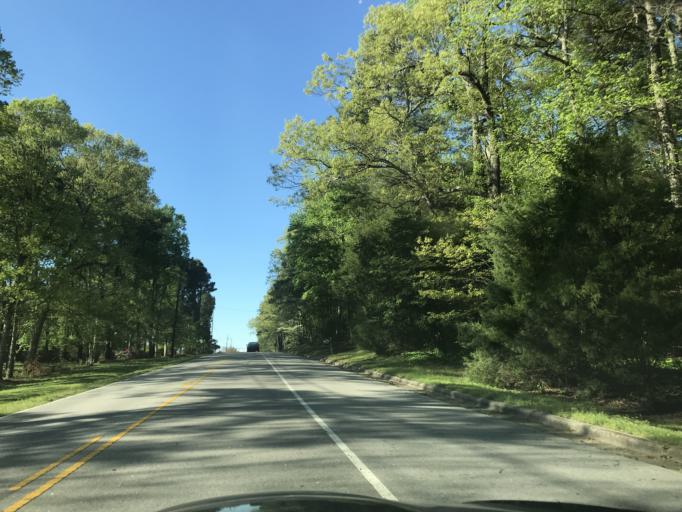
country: US
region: North Carolina
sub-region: Wake County
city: Knightdale
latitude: 35.8308
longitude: -78.5555
